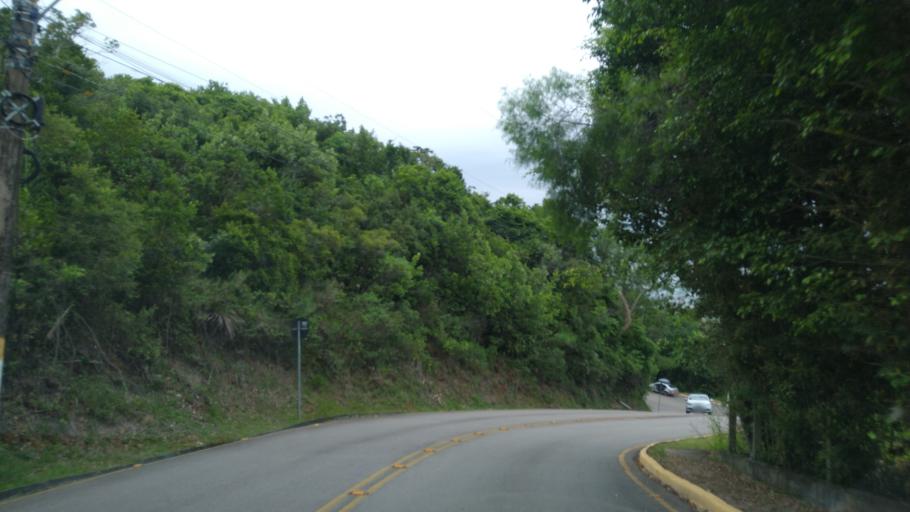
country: BR
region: Santa Catarina
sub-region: Itapema
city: Itapema
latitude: -27.0904
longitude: -48.6027
